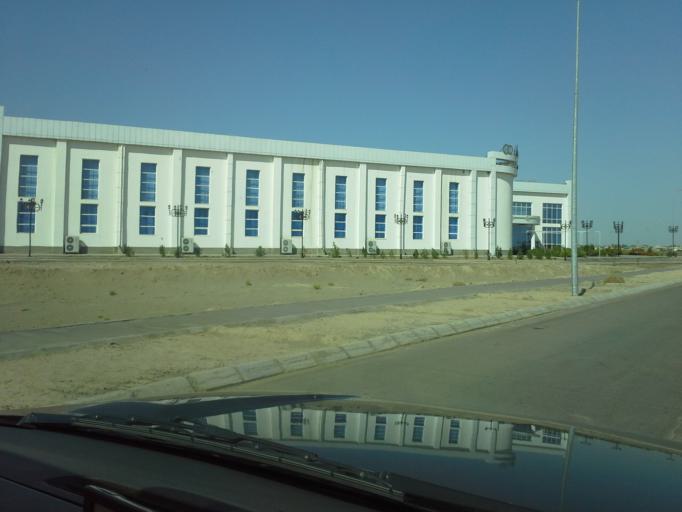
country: TM
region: Dasoguz
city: Dasoguz
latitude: 41.8041
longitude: 59.9530
